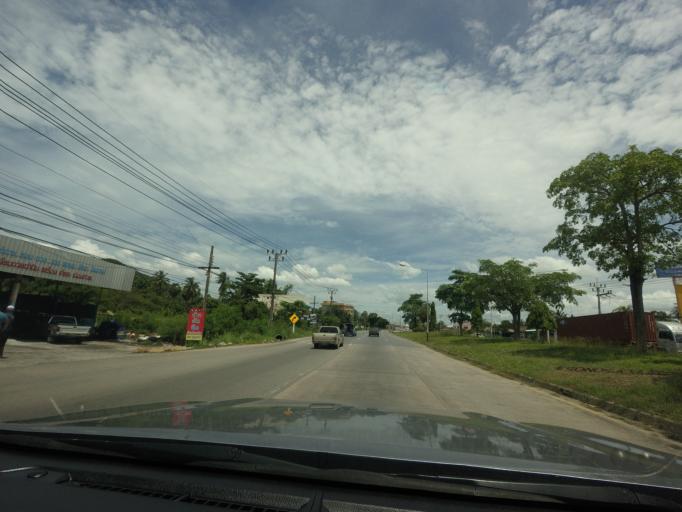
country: TH
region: Songkhla
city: Ban Mai
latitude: 7.2135
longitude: 100.5569
